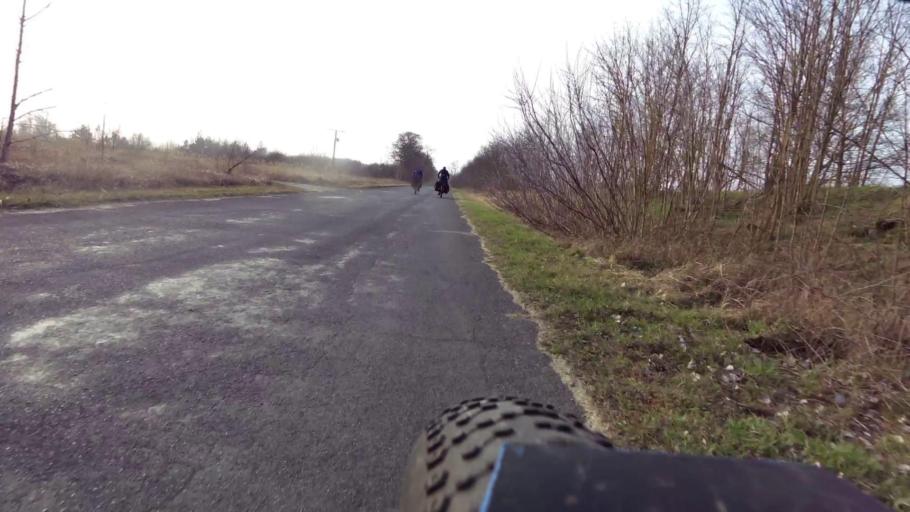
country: DE
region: Brandenburg
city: Vogelsang
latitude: 52.2555
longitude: 14.6995
